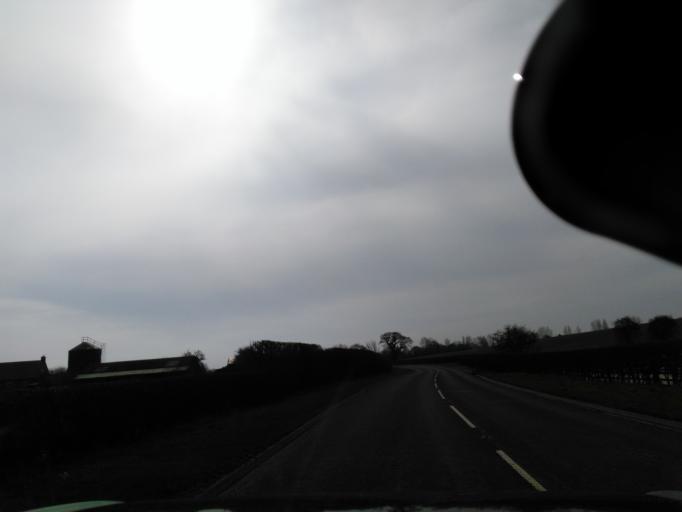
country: GB
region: England
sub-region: North Yorkshire
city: Thirsk
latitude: 54.2656
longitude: -1.3625
